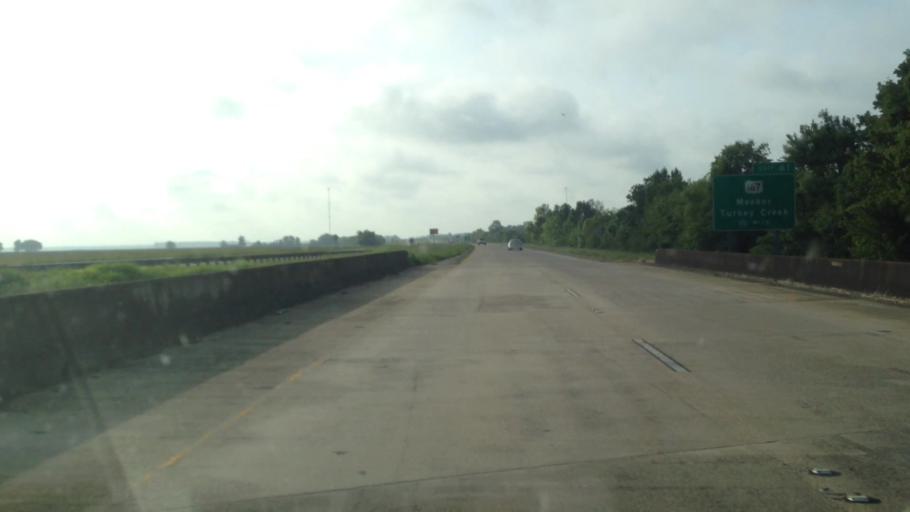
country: US
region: Louisiana
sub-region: Rapides Parish
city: Lecompte
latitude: 31.0199
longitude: -92.3892
